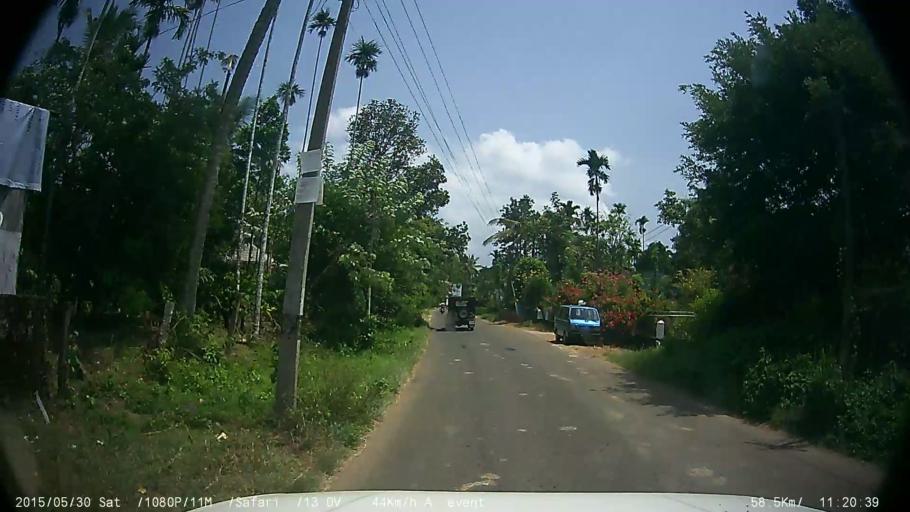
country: IN
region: Kerala
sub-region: Wayanad
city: Panamaram
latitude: 11.7971
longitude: 76.0391
